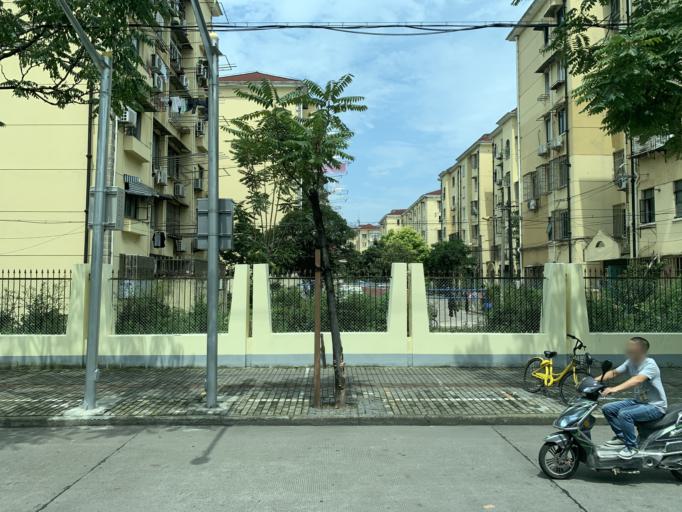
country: CN
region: Shanghai Shi
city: Huamu
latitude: 31.2489
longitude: 121.5757
